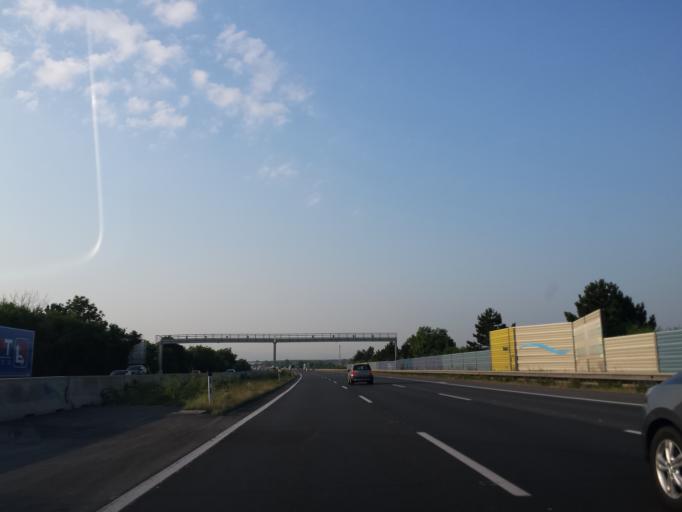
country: AT
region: Lower Austria
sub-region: Politischer Bezirk Wiener Neustadt
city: Weikersdorf am Steinfelde
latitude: 47.8295
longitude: 16.1841
